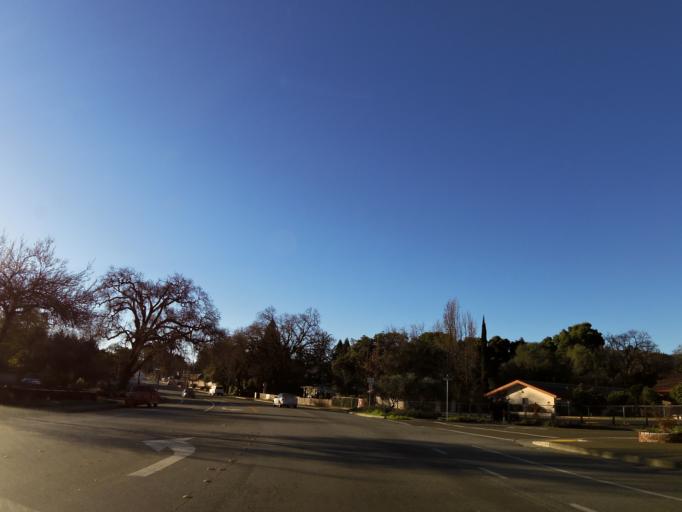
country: US
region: California
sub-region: Sonoma County
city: Cloverdale
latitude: 38.7976
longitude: -123.0188
